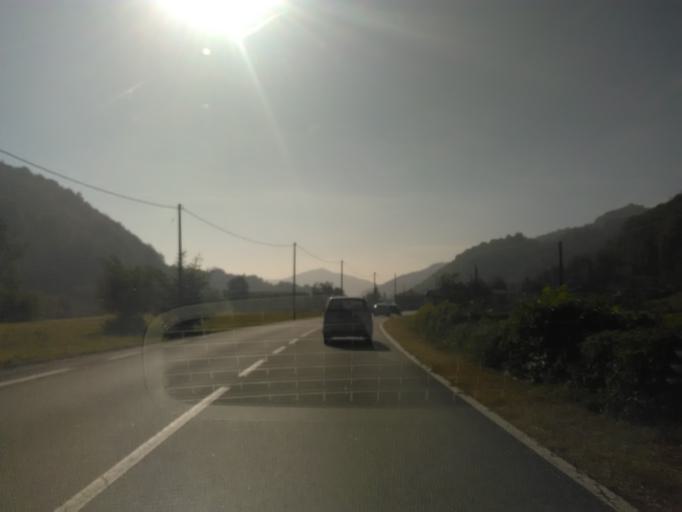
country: IT
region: Piedmont
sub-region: Provincia di Vercelli
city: Quarona
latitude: 45.7471
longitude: 8.2603
